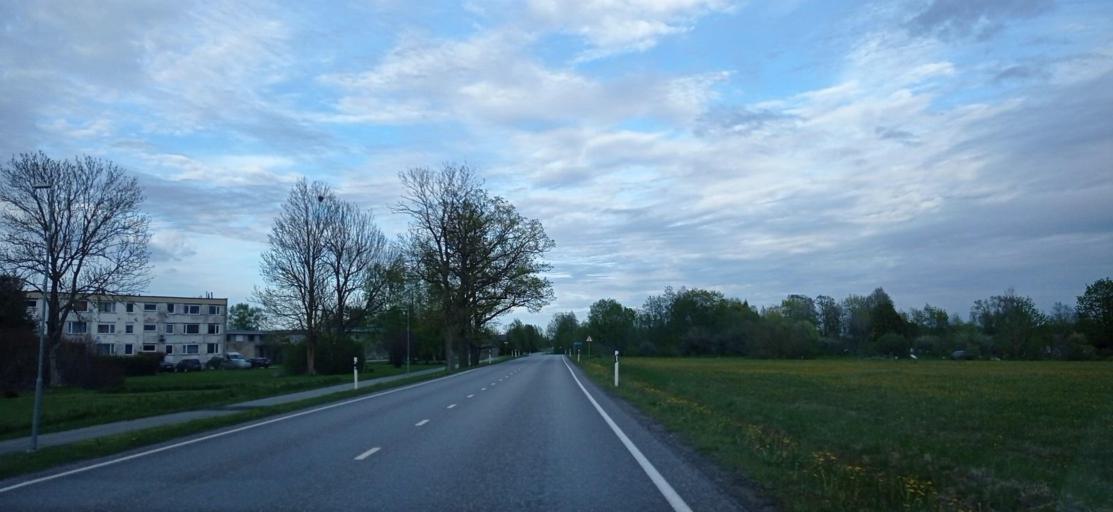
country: EE
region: Paernumaa
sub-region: Tootsi vald
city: Tootsi
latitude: 58.5267
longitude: 24.6986
